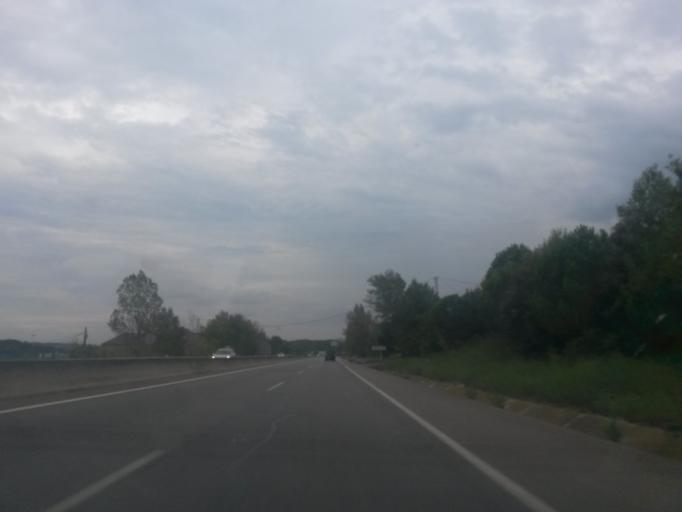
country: ES
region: Catalonia
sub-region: Provincia de Girona
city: Cornella del Terri
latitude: 42.0879
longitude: 2.8113
